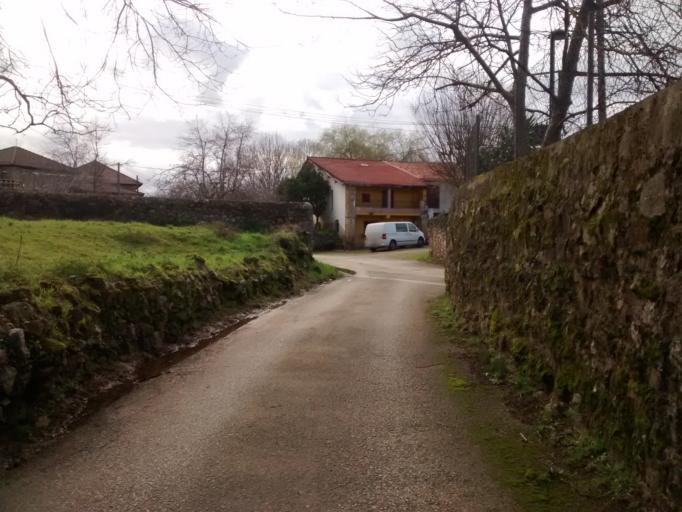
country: ES
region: Cantabria
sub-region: Provincia de Cantabria
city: Entrambasaguas
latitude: 43.3419
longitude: -3.6808
